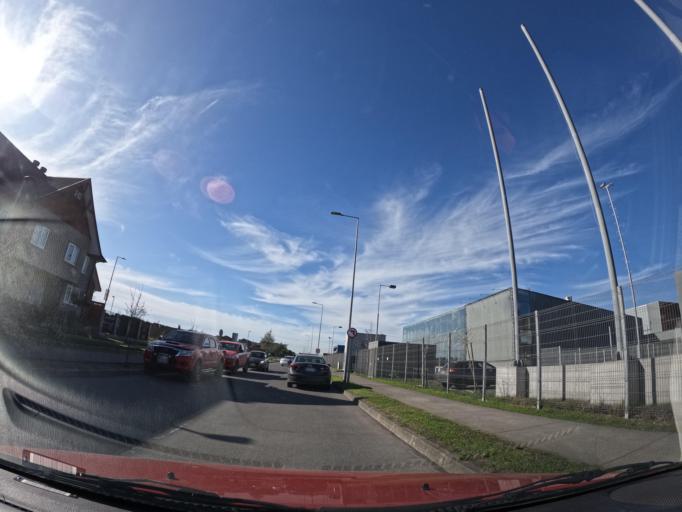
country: CL
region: Biobio
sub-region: Provincia de Concepcion
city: Concepcion
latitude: -36.7724
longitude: -73.0668
